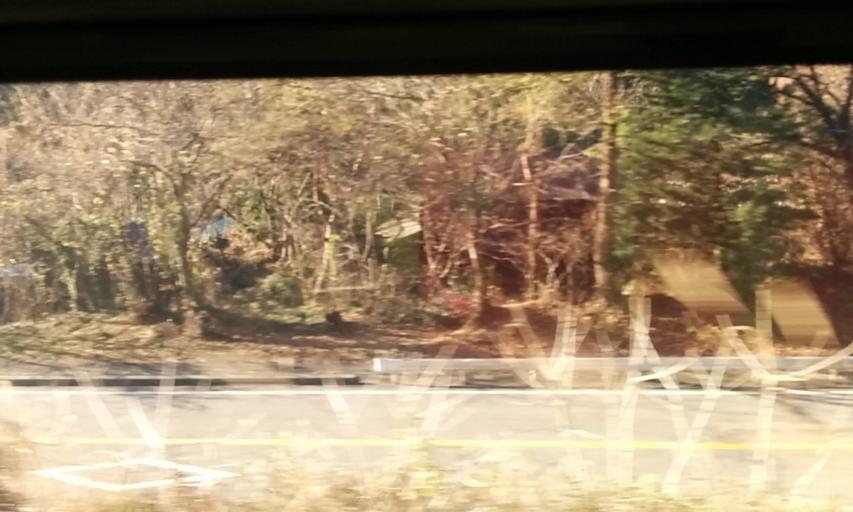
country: JP
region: Nagano
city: Iida
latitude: 35.7137
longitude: 137.7073
